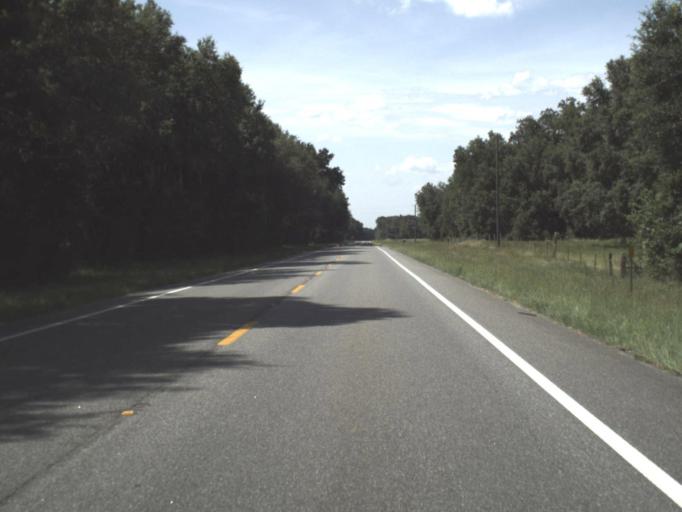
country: US
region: Florida
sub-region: Alachua County
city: High Springs
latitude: 29.8446
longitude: -82.7418
